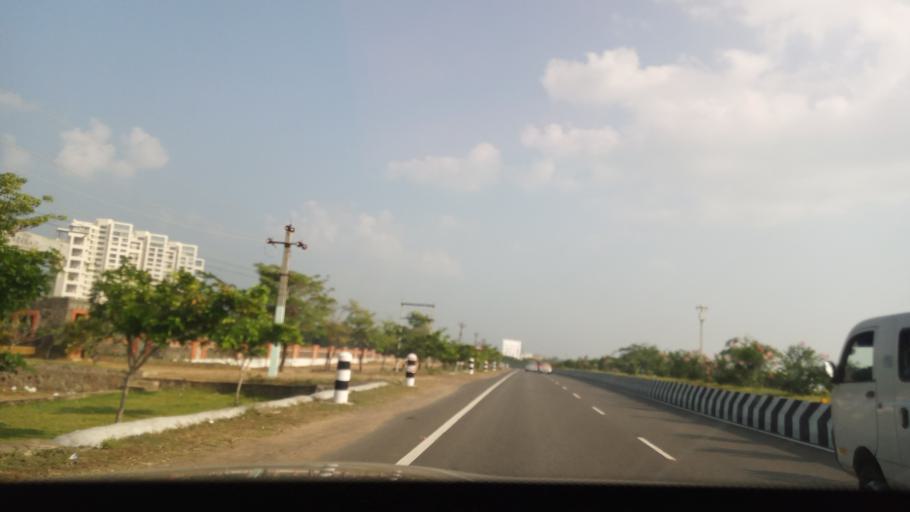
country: IN
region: Tamil Nadu
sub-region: Kancheepuram
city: Injambakkam
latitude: 12.7711
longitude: 80.2481
